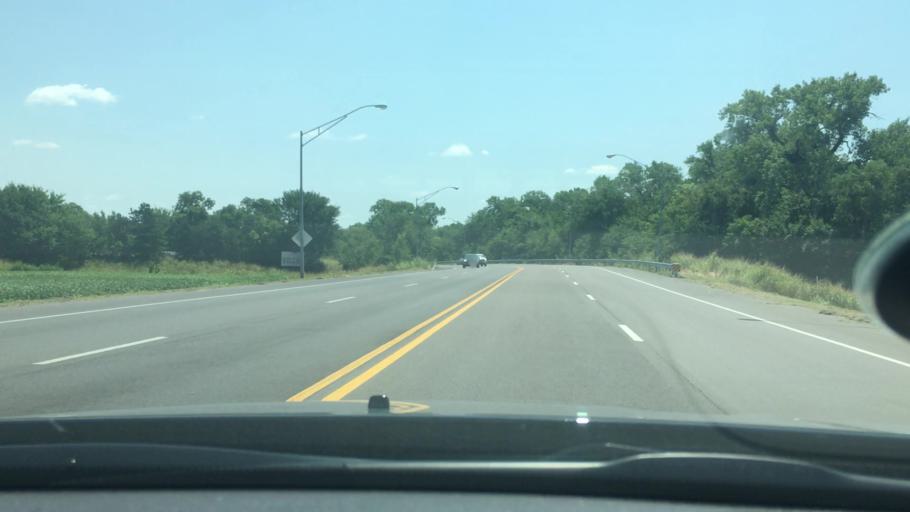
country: US
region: Oklahoma
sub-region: Garvin County
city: Pauls Valley
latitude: 34.7364
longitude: -97.2318
